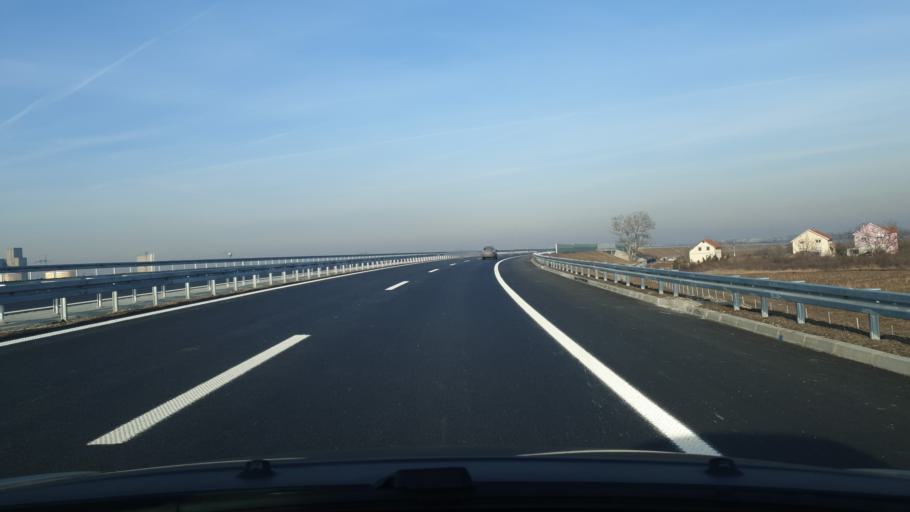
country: RS
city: Becmen
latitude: 44.7631
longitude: 20.2458
